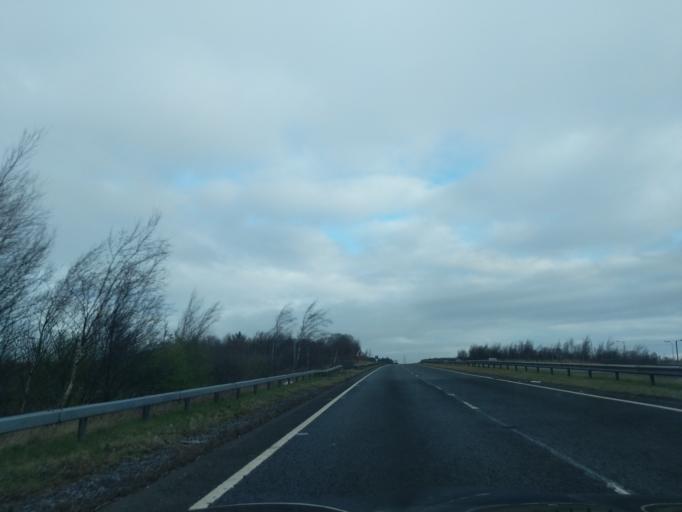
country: GB
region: England
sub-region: Northumberland
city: Stannington
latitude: 55.1133
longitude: -1.6669
